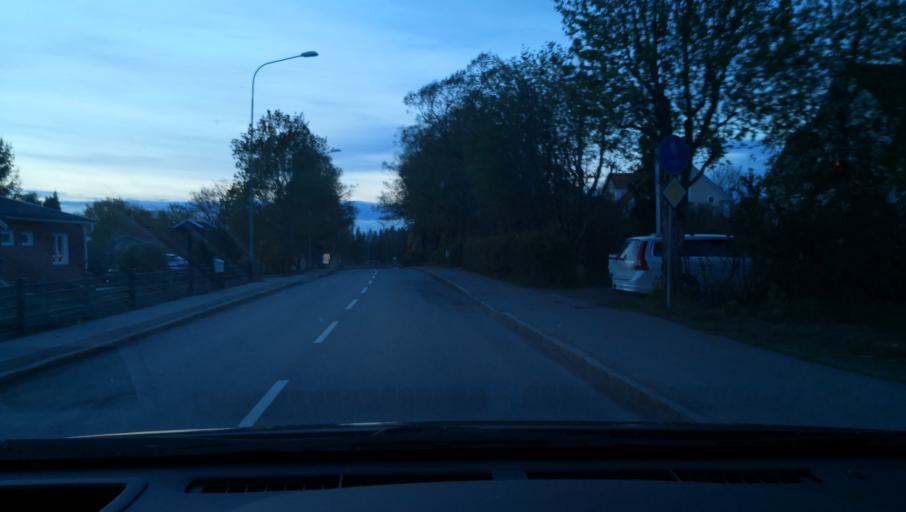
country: SE
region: OErebro
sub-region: Lekebergs Kommun
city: Fjugesta
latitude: 59.0259
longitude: 14.8670
